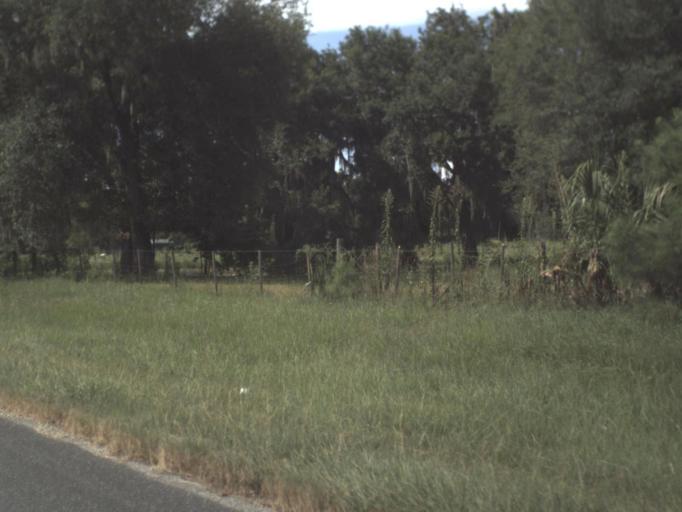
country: US
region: Florida
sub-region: Taylor County
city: Perry
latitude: 30.1798
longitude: -83.6000
